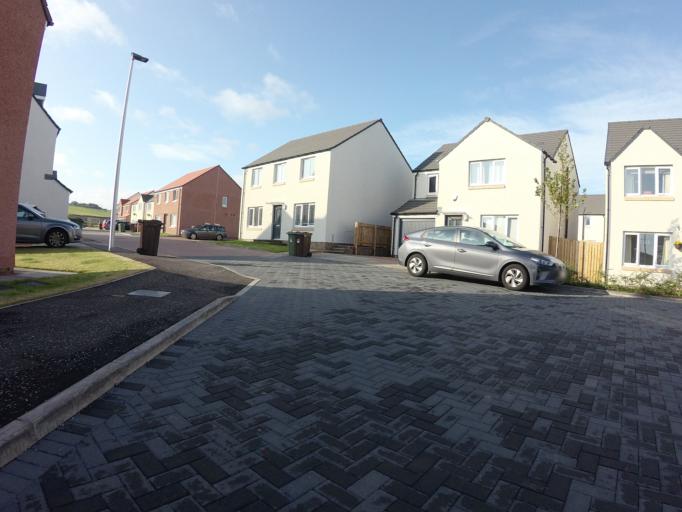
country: GB
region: Scotland
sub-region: East Lothian
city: Prestonpans
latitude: 55.9403
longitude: -3.0020
